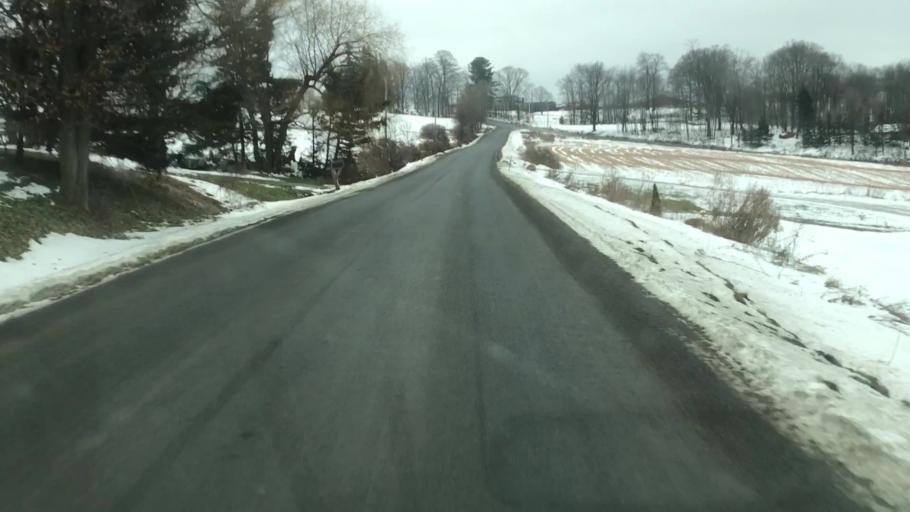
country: US
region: New York
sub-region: Cortland County
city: Cortland West
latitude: 42.6479
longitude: -76.2571
